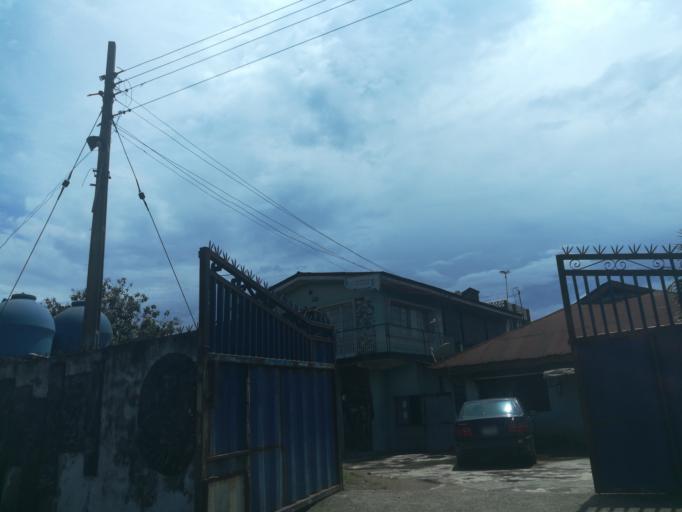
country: NG
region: Lagos
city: Agege
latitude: 6.6187
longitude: 3.3287
